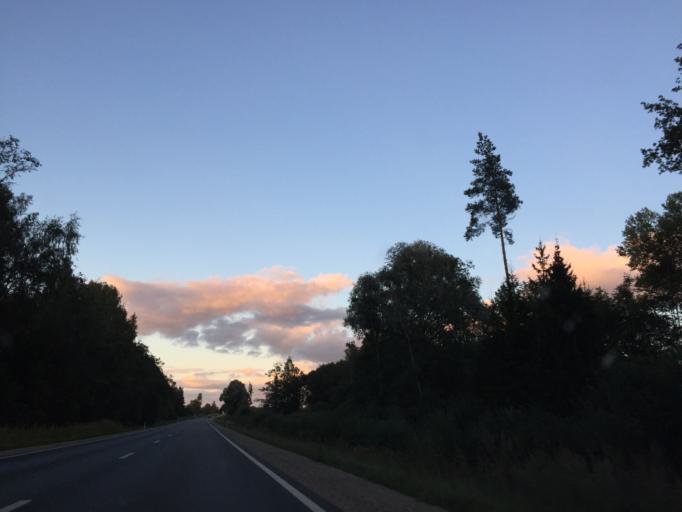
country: LV
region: Jaunpils
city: Jaunpils
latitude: 56.6976
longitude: 23.1474
